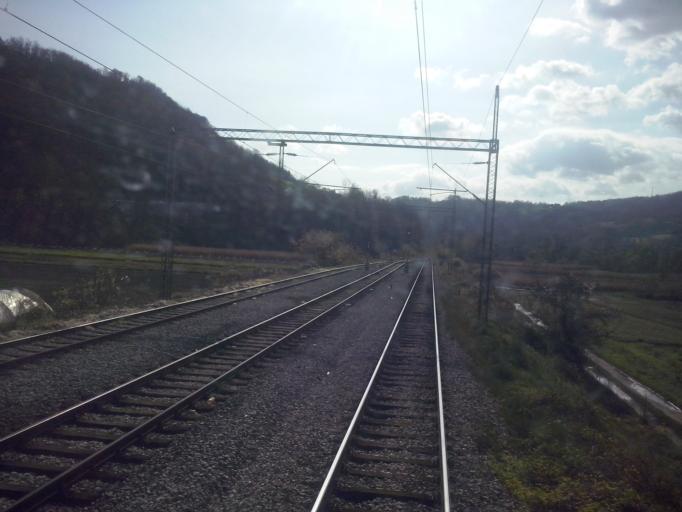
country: RS
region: Central Serbia
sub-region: Zlatiborski Okrug
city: Pozega
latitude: 43.9258
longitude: 19.9899
